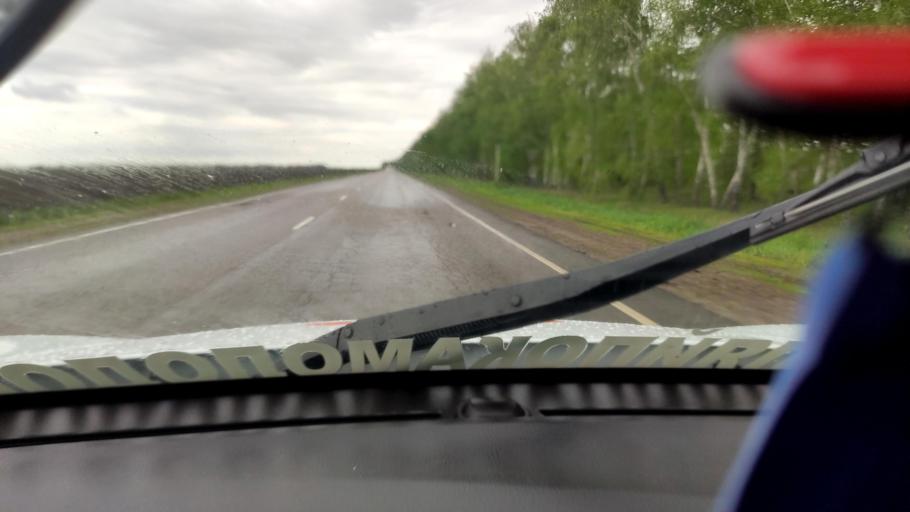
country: RU
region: Voronezj
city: Sredniy Ikorets
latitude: 51.0383
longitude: 39.6498
